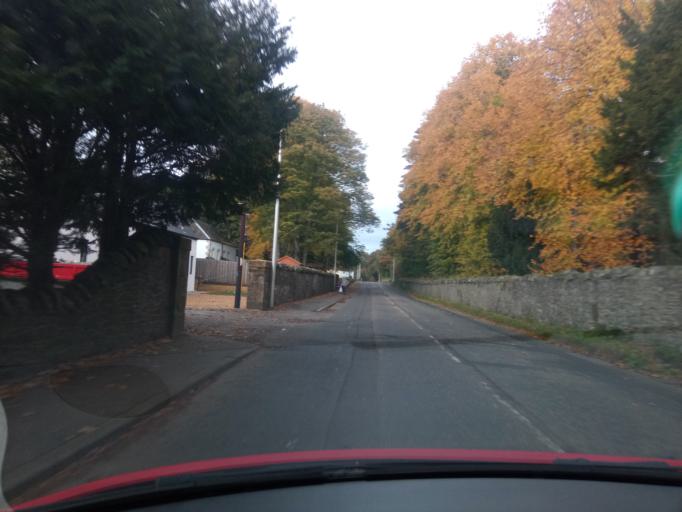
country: GB
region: Scotland
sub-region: The Scottish Borders
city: Peebles
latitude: 55.6461
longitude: -3.1780
